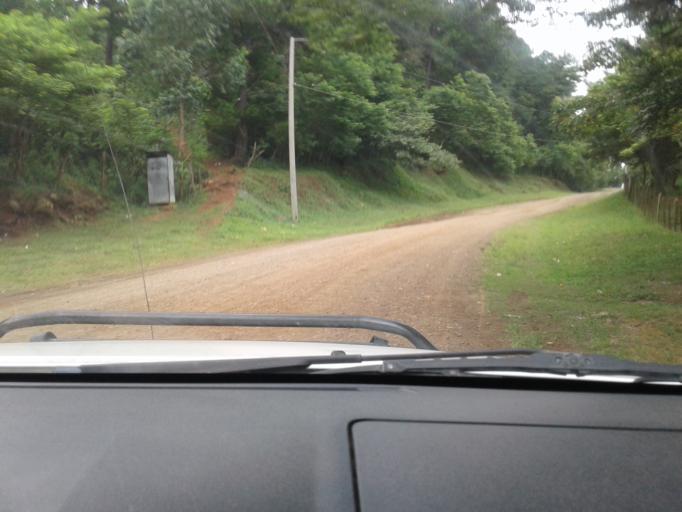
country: NI
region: Matagalpa
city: San Ramon
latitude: 12.9102
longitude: -85.7733
